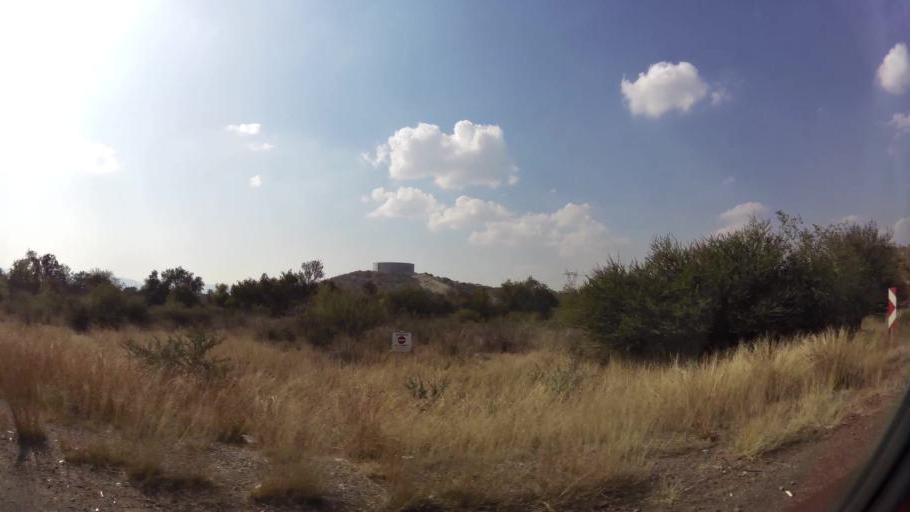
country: ZA
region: North-West
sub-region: Bojanala Platinum District Municipality
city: Mogwase
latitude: -25.4364
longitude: 27.0862
